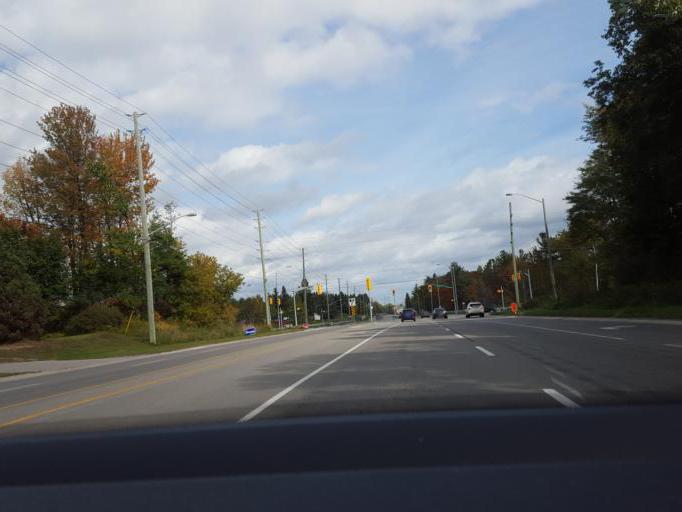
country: CA
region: Ontario
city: Ajax
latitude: 43.8883
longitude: -79.0716
